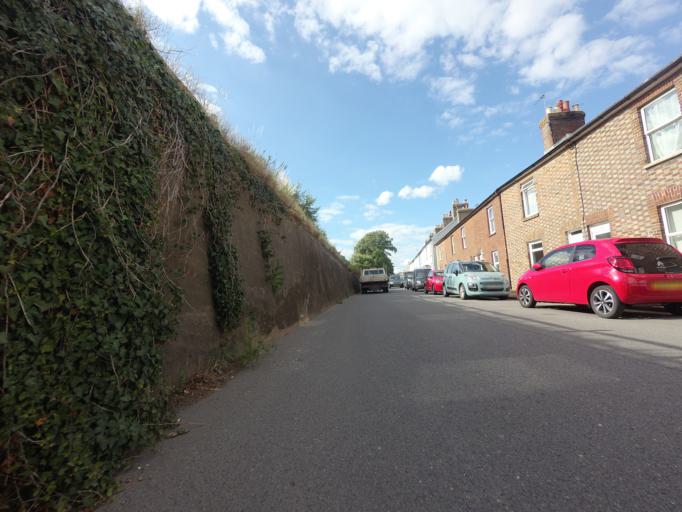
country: GB
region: England
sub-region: East Sussex
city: Hailsham
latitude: 50.8596
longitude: 0.2576
